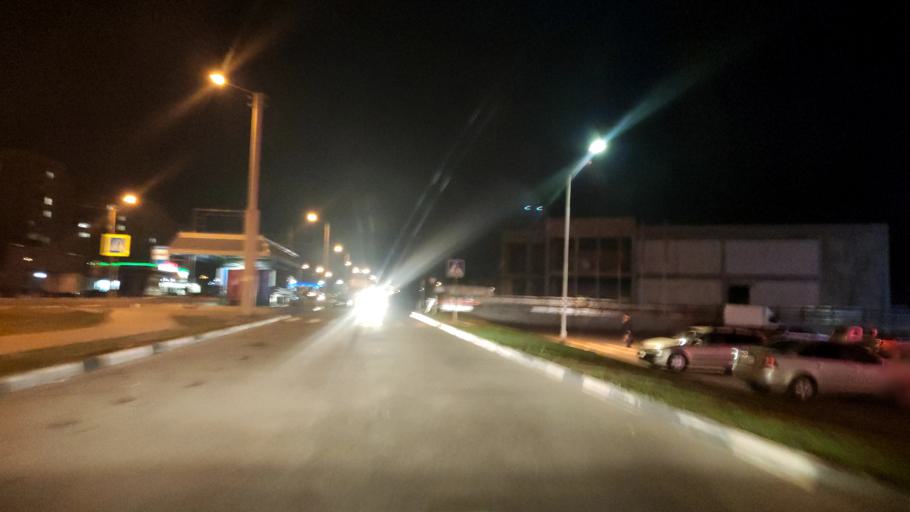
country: RU
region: Belgorod
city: Staryy Oskol
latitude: 51.2855
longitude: 37.7943
